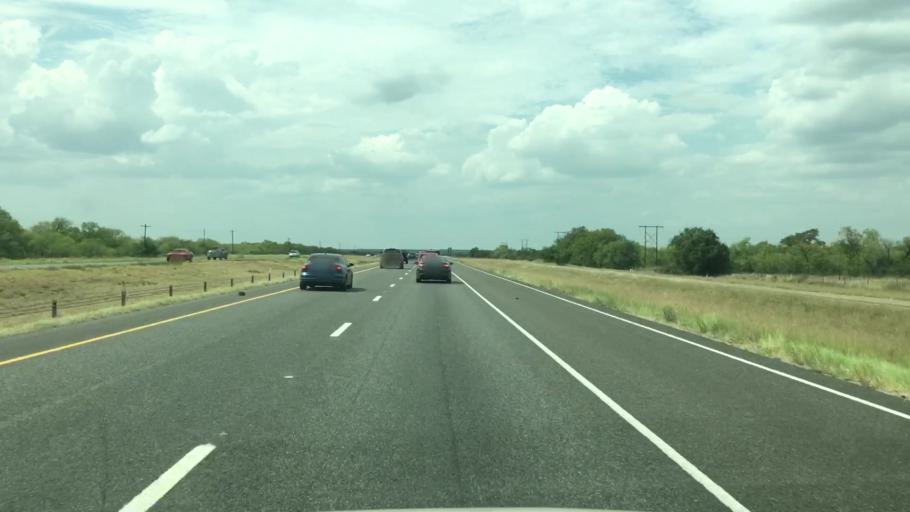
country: US
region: Texas
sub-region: Atascosa County
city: Pleasanton
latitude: 28.8227
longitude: -98.3629
